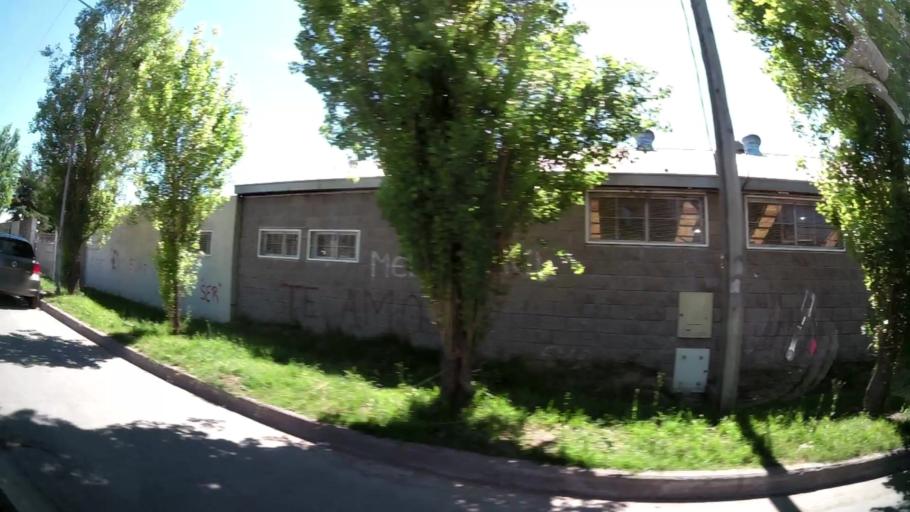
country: AR
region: Buenos Aires
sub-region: Partido de Tigre
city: Tigre
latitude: -34.4960
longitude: -58.6095
